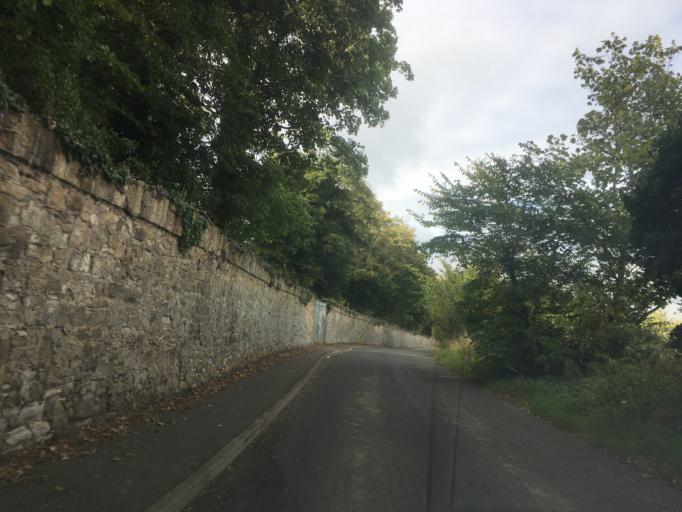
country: GB
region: Scotland
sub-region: East Lothian
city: Musselburgh
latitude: 55.9204
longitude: -3.0423
